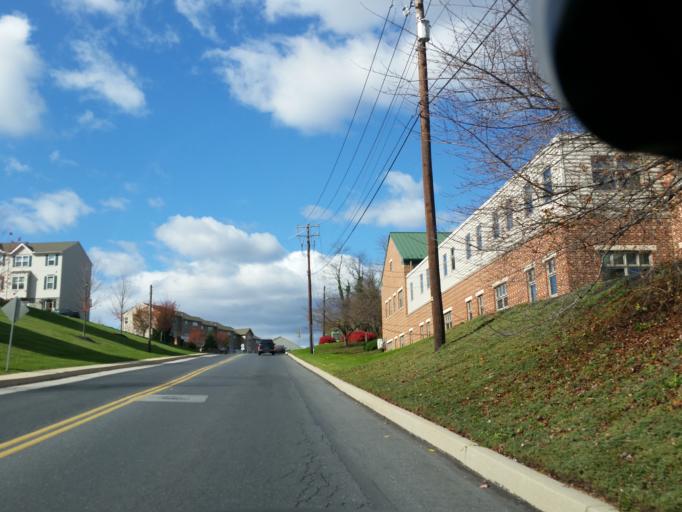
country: US
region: Pennsylvania
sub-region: Cumberland County
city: Camp Hill
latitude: 40.2434
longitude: -76.9098
